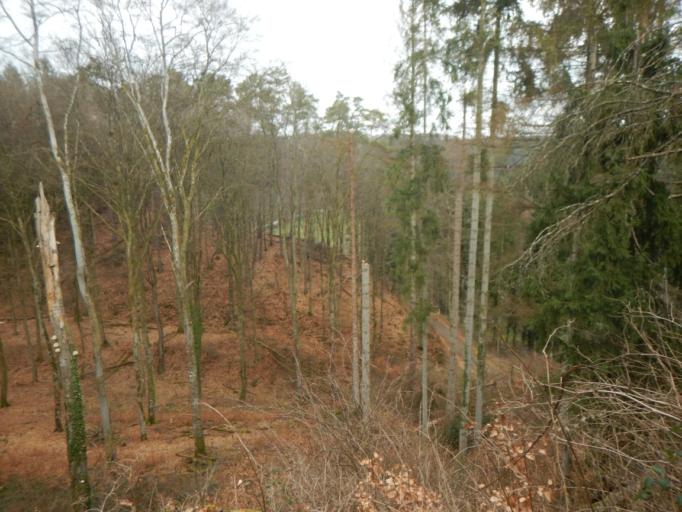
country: LU
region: Luxembourg
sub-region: Canton de Capellen
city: Kehlen
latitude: 49.7102
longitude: 6.0563
